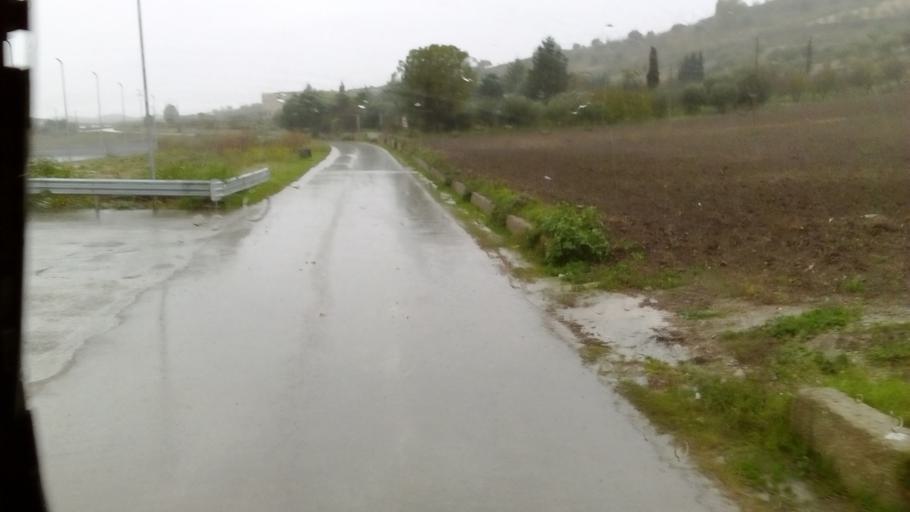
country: IT
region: Sicily
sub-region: Enna
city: Pietraperzia
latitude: 37.4040
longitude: 14.1418
